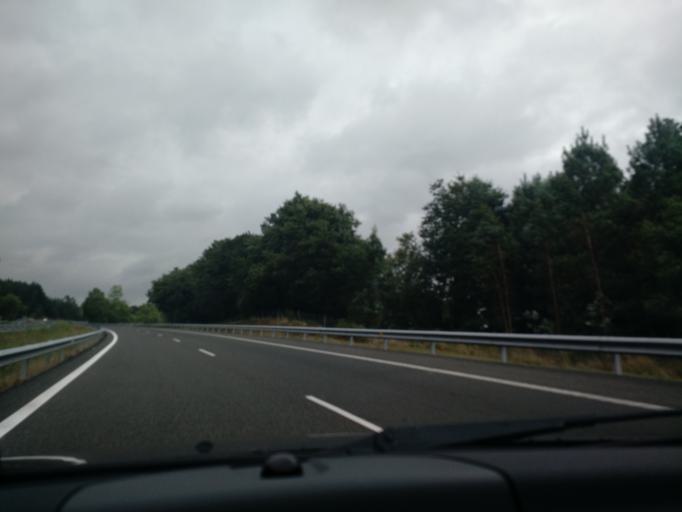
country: ES
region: Galicia
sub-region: Provincia da Coruna
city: Oroso
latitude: 43.0051
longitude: -8.4195
